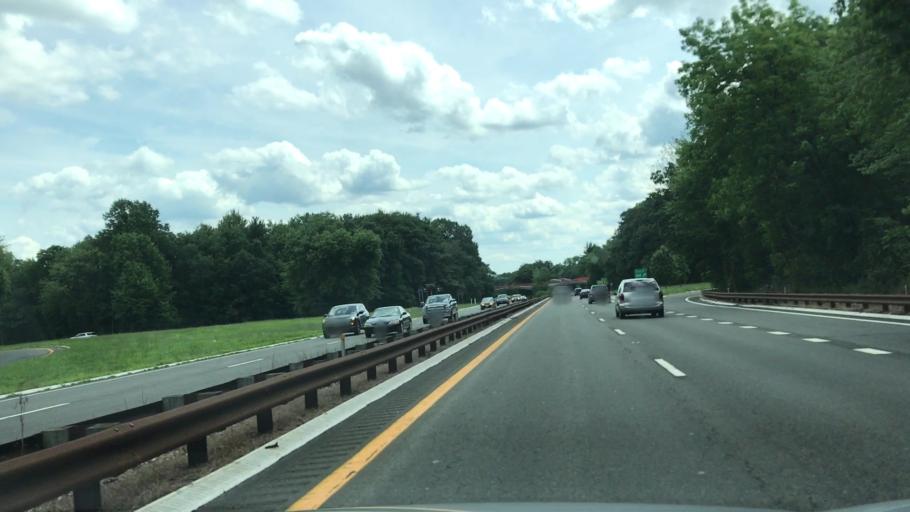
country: US
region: New York
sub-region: Rockland County
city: Bardonia
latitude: 41.0940
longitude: -73.9910
